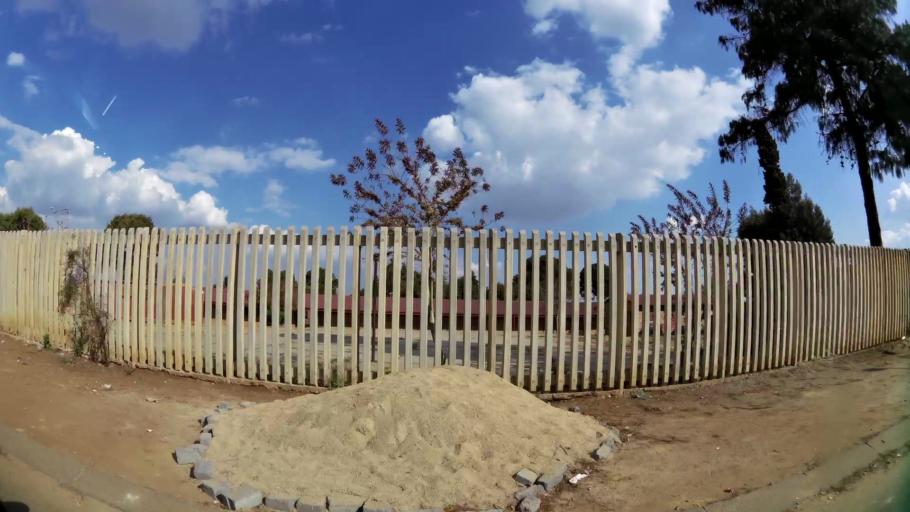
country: ZA
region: Gauteng
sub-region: City of Johannesburg Metropolitan Municipality
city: Soweto
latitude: -26.2209
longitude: 27.8605
